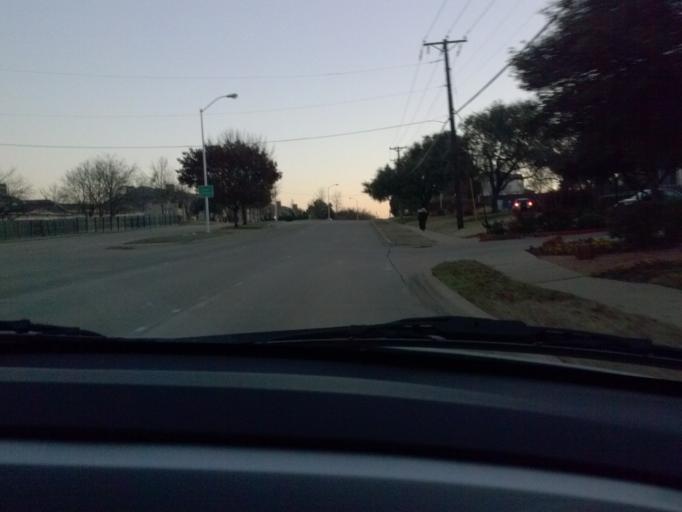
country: US
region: Texas
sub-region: Collin County
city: Allen
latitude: 33.0740
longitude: -96.7098
